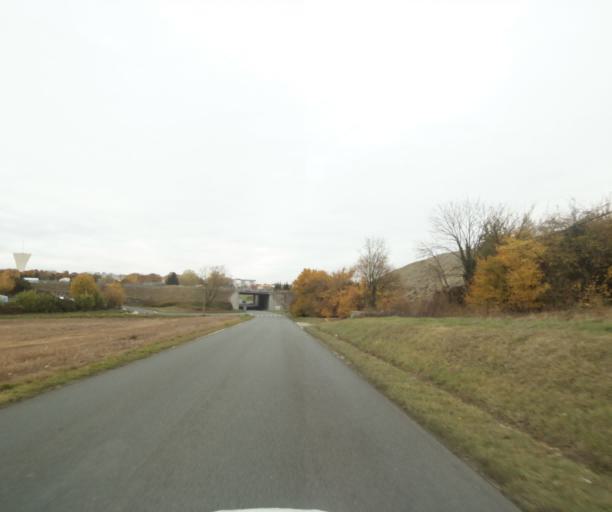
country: FR
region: Poitou-Charentes
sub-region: Departement de la Charente-Maritime
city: Saintes
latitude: 45.7253
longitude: -0.6529
